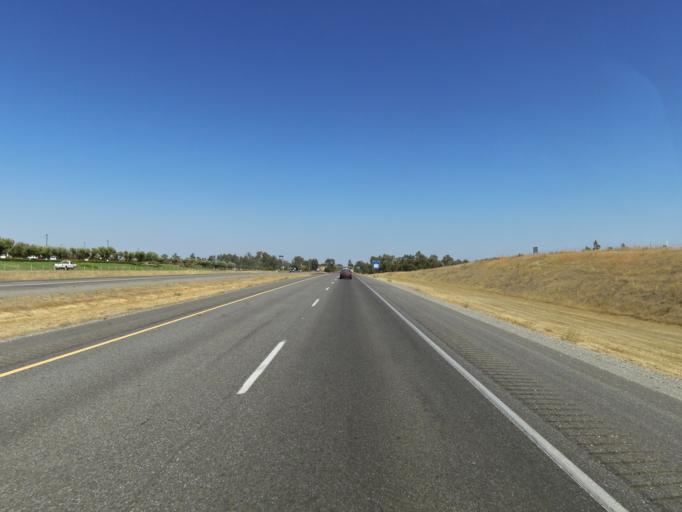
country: US
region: California
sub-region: Tehama County
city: Corning
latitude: 39.8732
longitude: -122.1999
